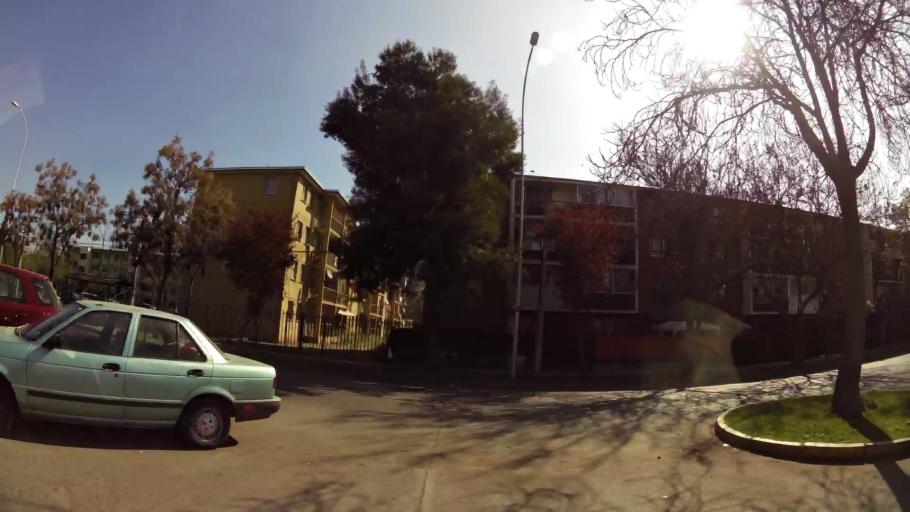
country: CL
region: Santiago Metropolitan
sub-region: Provincia de Santiago
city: Santiago
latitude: -33.4693
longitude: -70.6218
